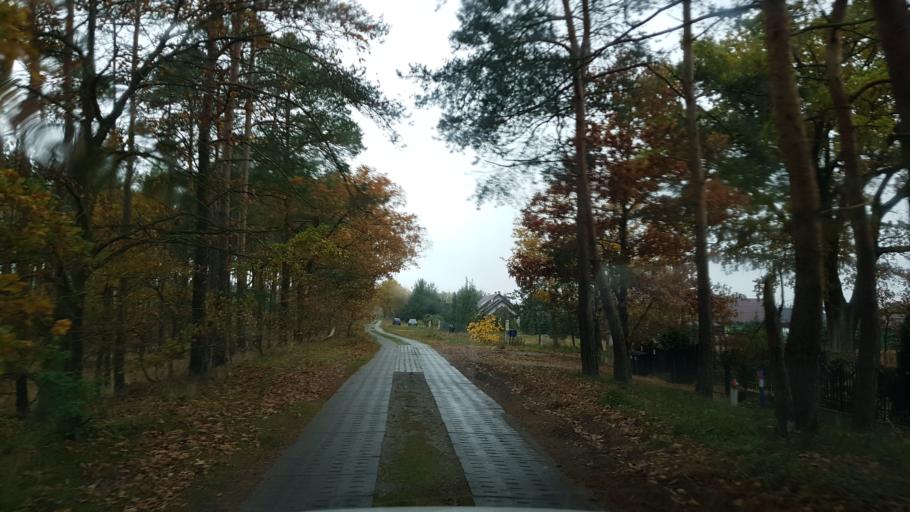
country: PL
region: West Pomeranian Voivodeship
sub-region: Powiat goleniowski
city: Goleniow
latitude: 53.5801
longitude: 14.7825
